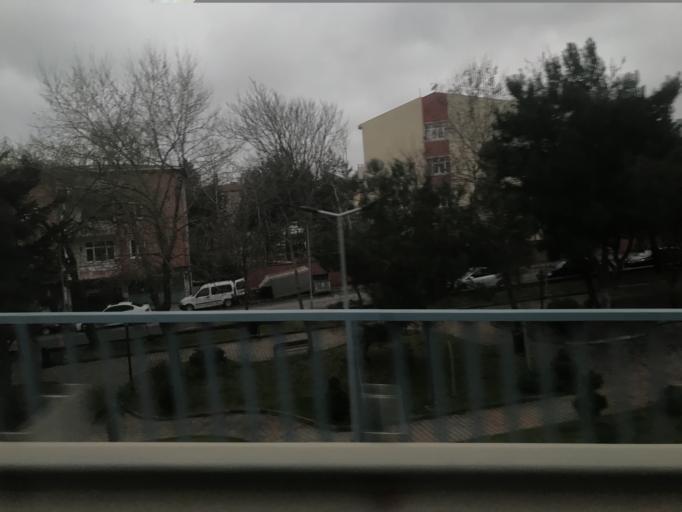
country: TR
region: Istanbul
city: Maltepe
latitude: 40.9143
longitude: 29.1700
